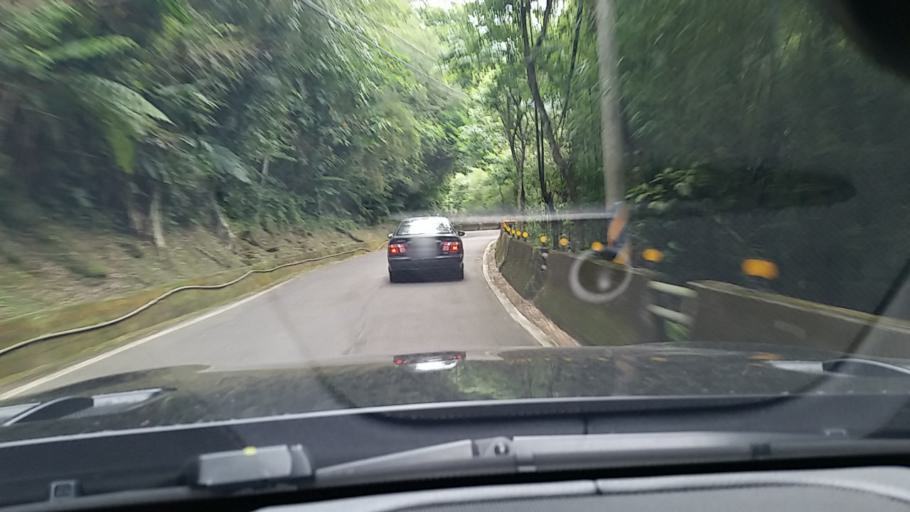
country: TW
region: Taiwan
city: Daxi
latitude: 24.7990
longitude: 121.3032
